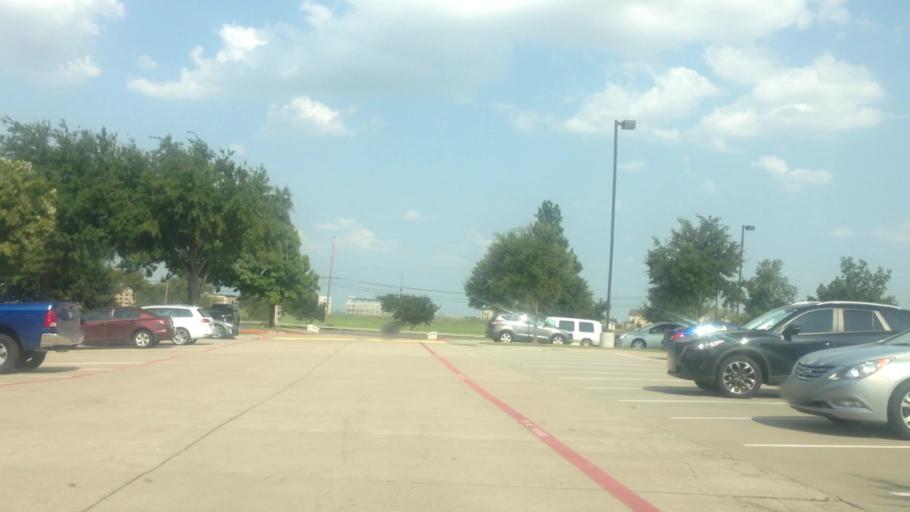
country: US
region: Texas
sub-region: Dallas County
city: Coppell
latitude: 32.9369
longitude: -96.9950
